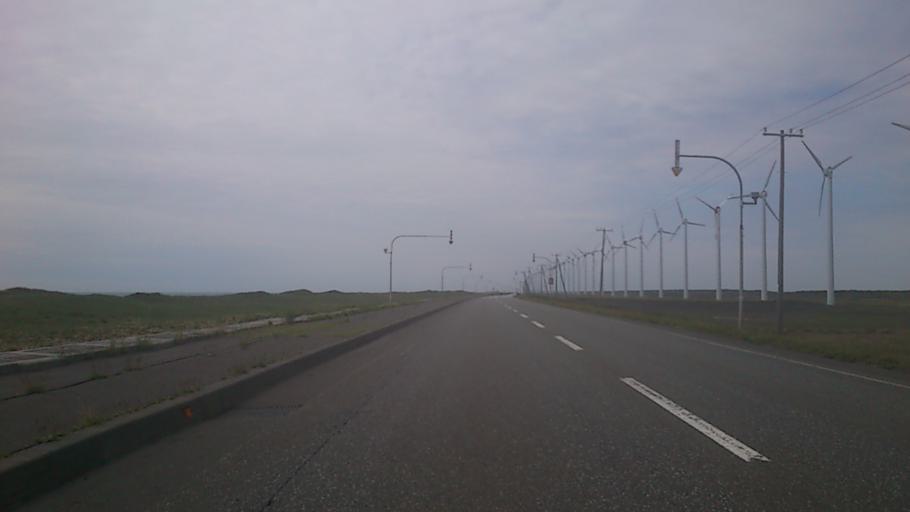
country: JP
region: Hokkaido
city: Makubetsu
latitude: 44.9546
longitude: 141.7073
